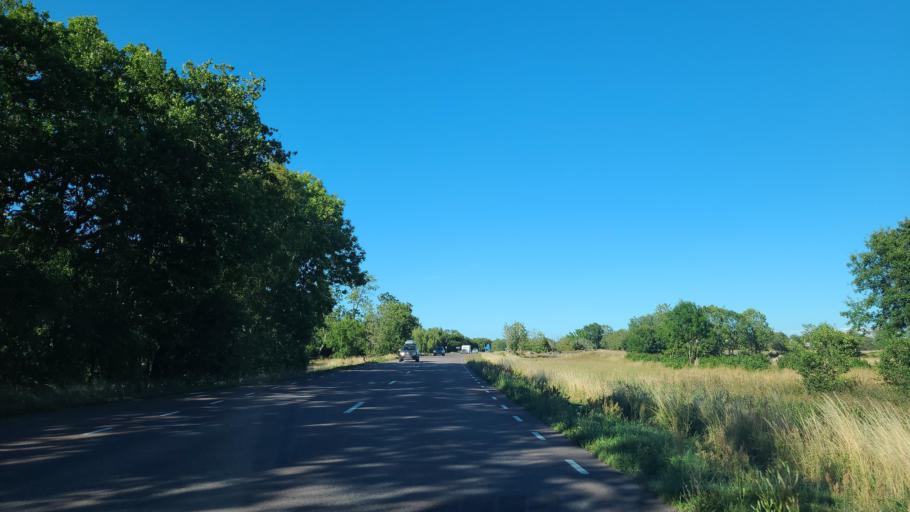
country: SE
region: Kalmar
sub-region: Borgholms Kommun
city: Borgholm
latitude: 57.1910
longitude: 17.0325
